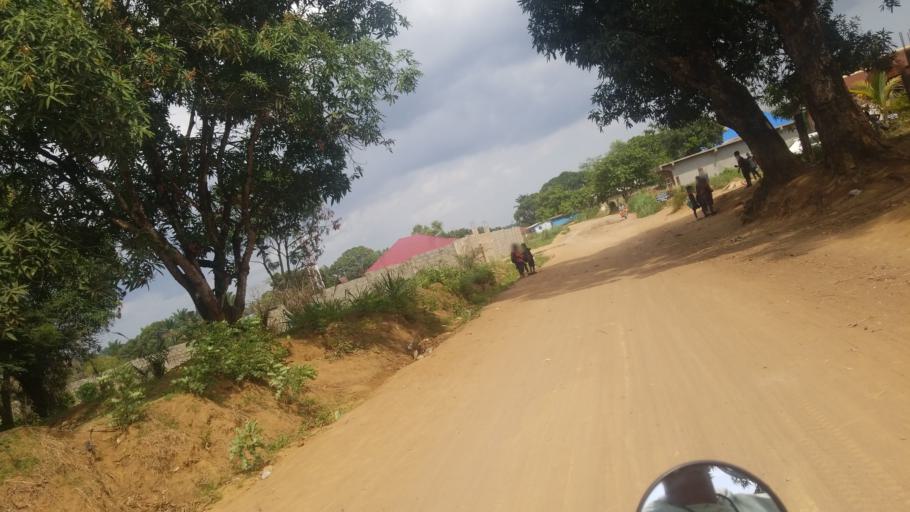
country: SL
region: Western Area
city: Waterloo
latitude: 8.3261
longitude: -13.0384
